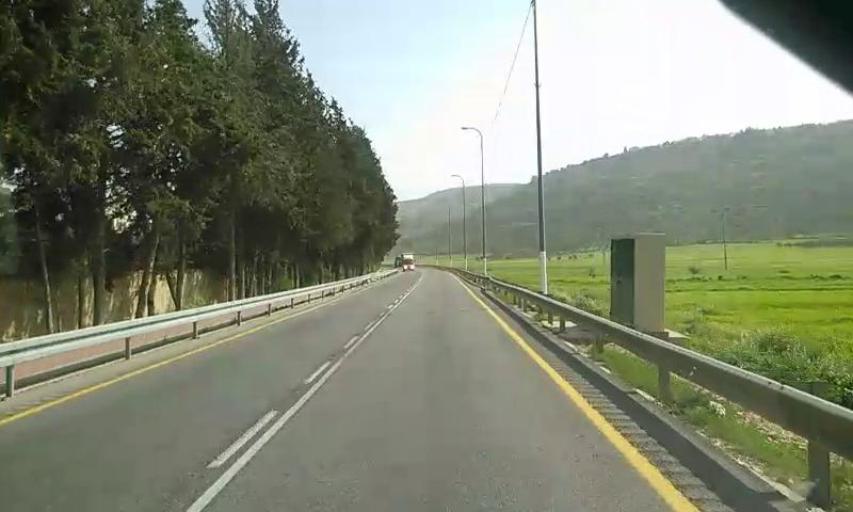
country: PS
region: West Bank
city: As Sawiyah
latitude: 32.0791
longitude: 35.2588
